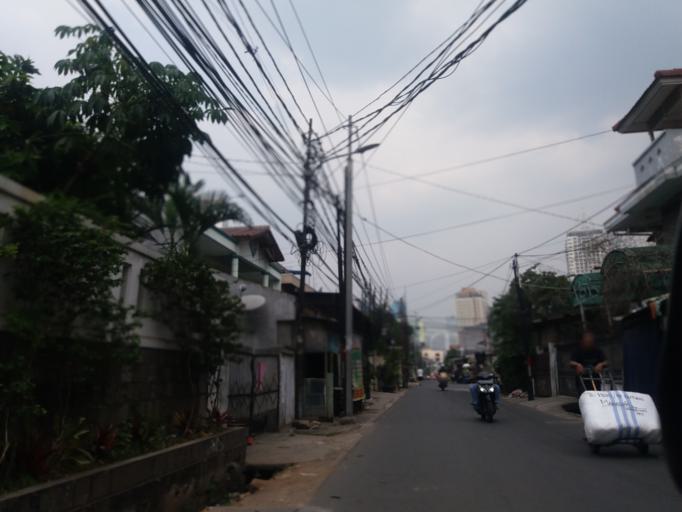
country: ID
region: Jakarta Raya
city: Jakarta
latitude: -6.1891
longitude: 106.8187
